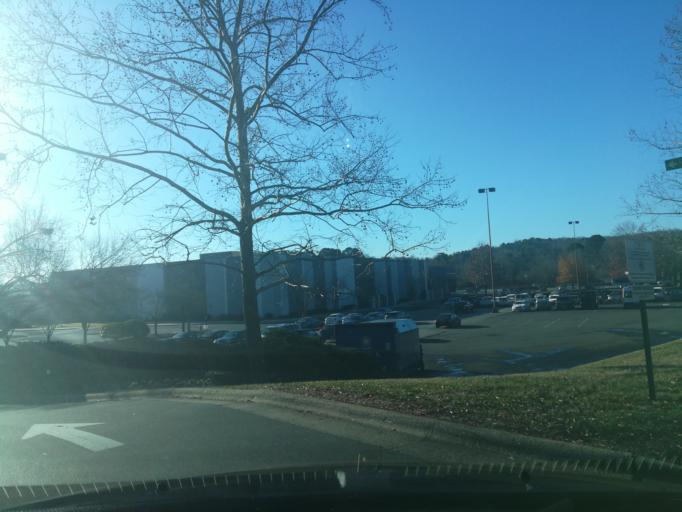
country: US
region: North Carolina
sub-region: Orange County
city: Chapel Hill
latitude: 35.9297
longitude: -79.0282
